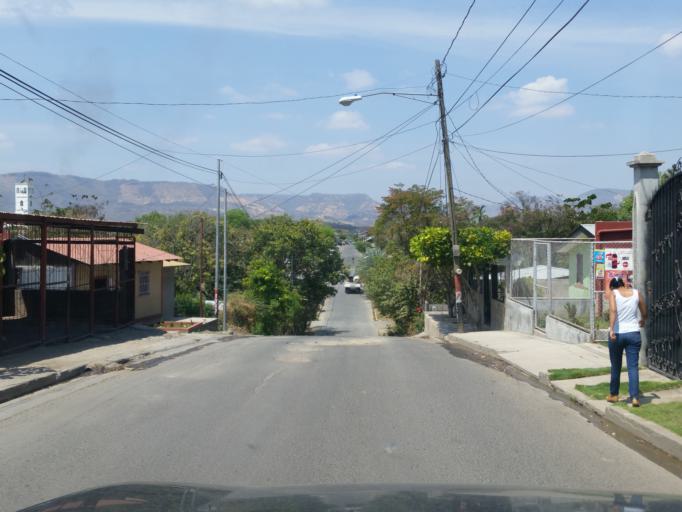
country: NI
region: Matagalpa
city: Ciudad Dario
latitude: 12.7296
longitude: -86.1199
